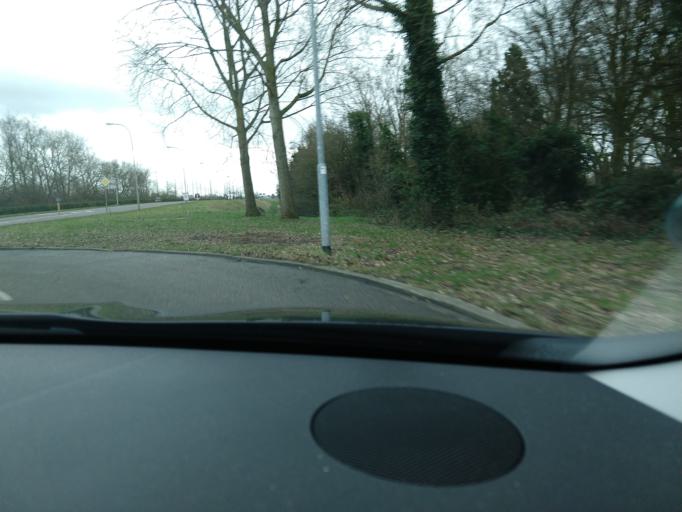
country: NL
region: Zeeland
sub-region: Gemeente Middelburg
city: Middelburg
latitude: 51.4975
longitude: 3.6292
